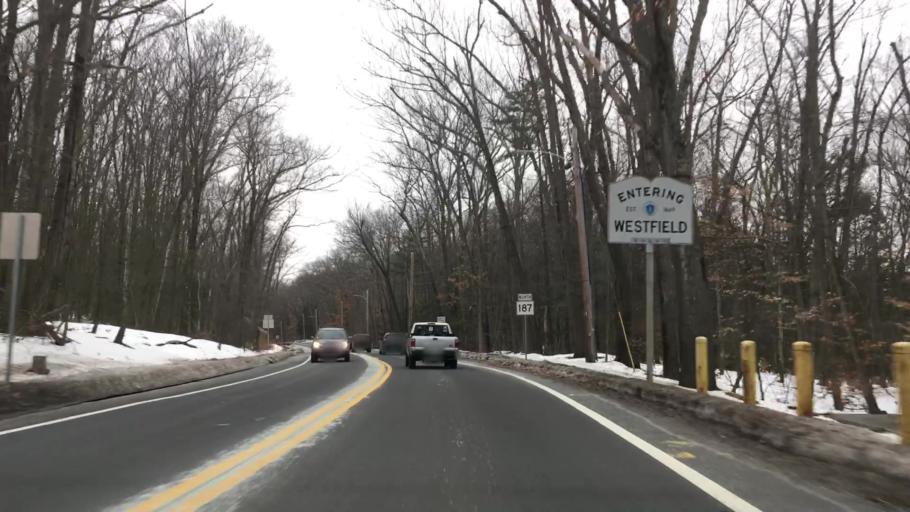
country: US
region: Massachusetts
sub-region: Hampden County
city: Westfield
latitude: 42.1048
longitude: -72.6953
